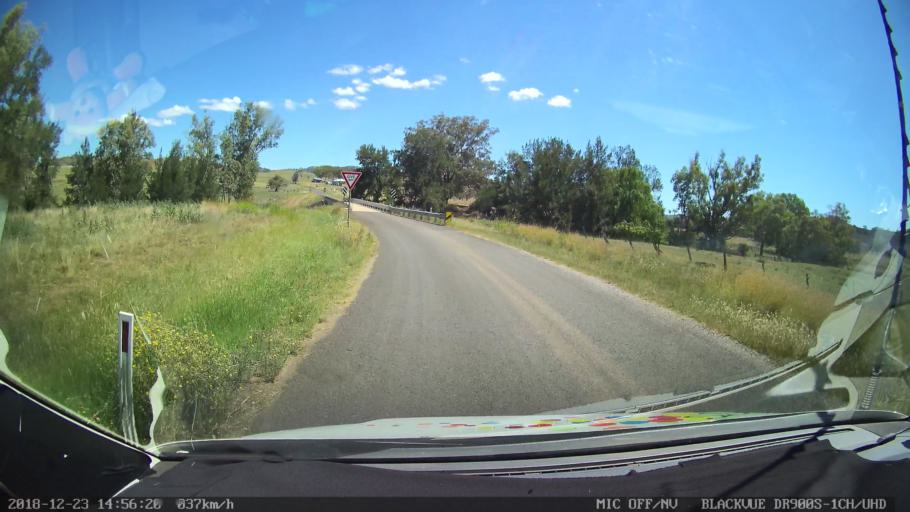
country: AU
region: New South Wales
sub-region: Tamworth Municipality
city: Manilla
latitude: -30.7034
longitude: 150.8298
